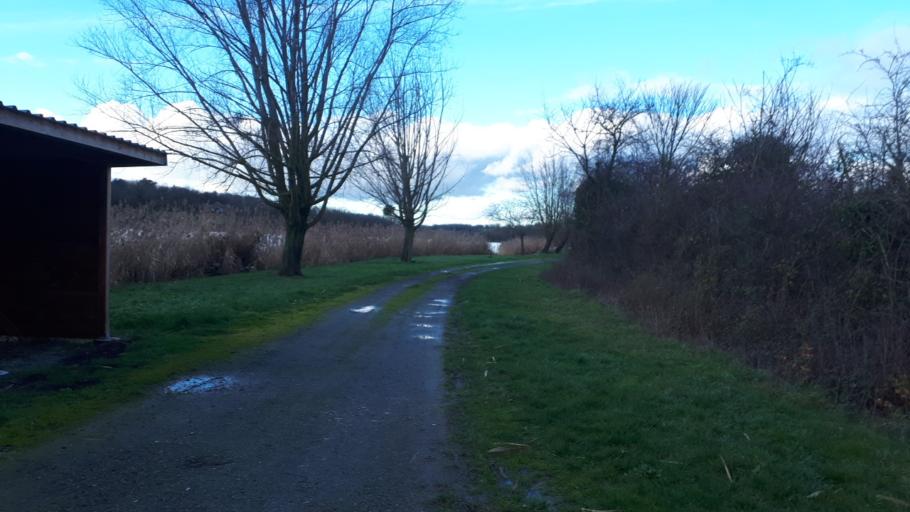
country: FR
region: Poitou-Charentes
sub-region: Departement de la Vienne
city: Pleumartin
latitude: 46.6326
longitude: 0.7667
